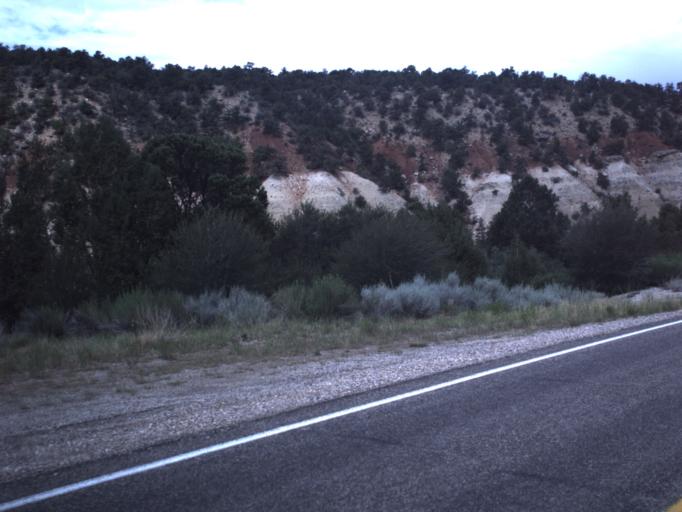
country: US
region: Utah
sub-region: Iron County
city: Cedar City
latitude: 37.6590
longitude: -112.9940
